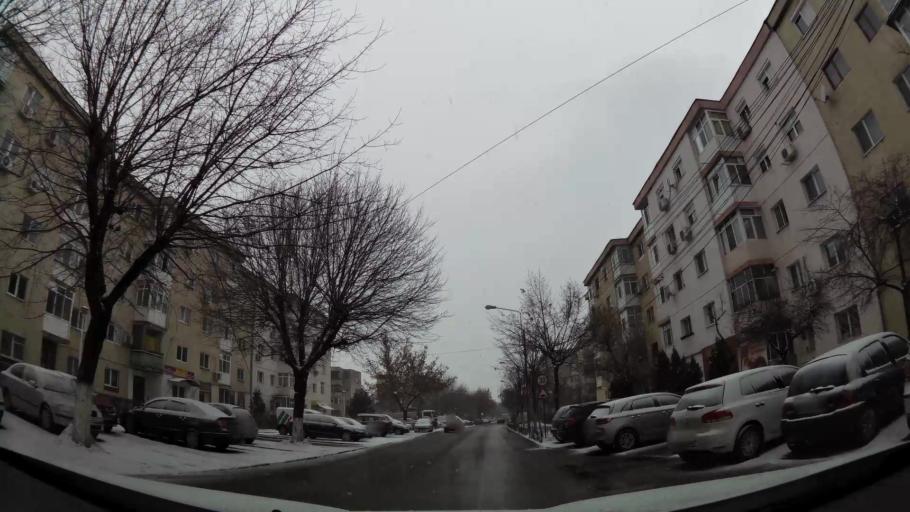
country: RO
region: Prahova
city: Ploiesti
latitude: 44.9305
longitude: 26.0033
